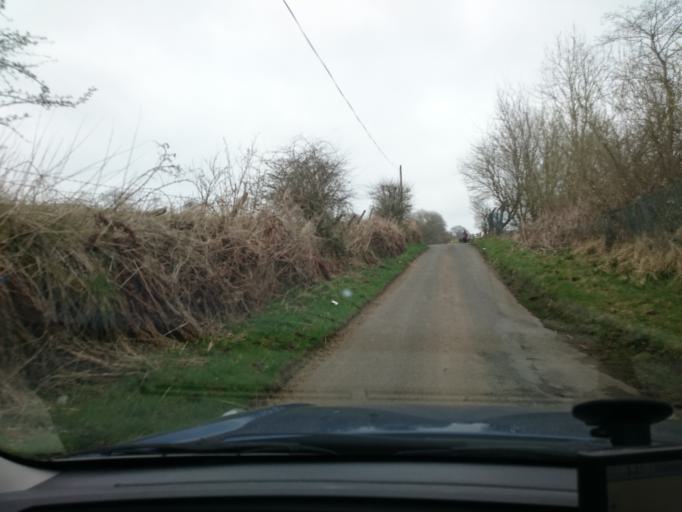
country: GB
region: Scotland
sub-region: Falkirk
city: Dunipace
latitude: 55.9954
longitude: -3.9546
